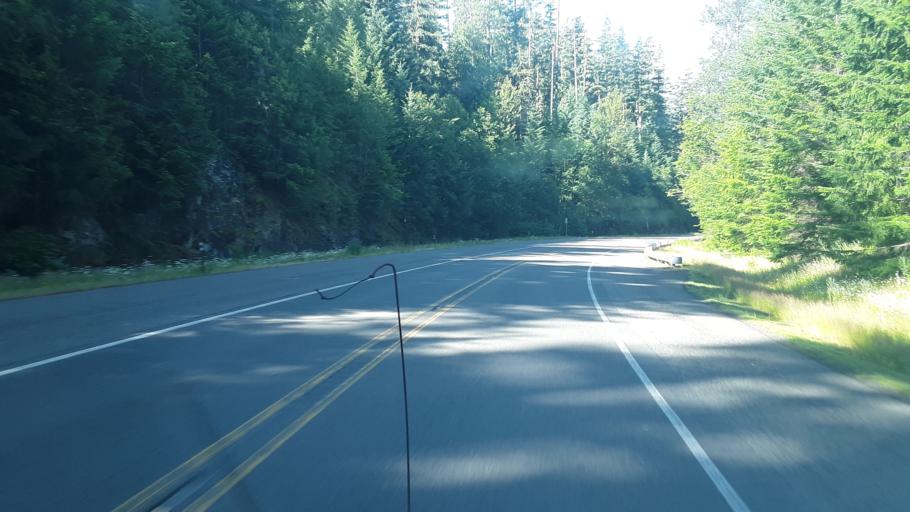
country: US
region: Washington
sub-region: Pierce County
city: Buckley
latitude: 46.6745
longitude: -121.5777
